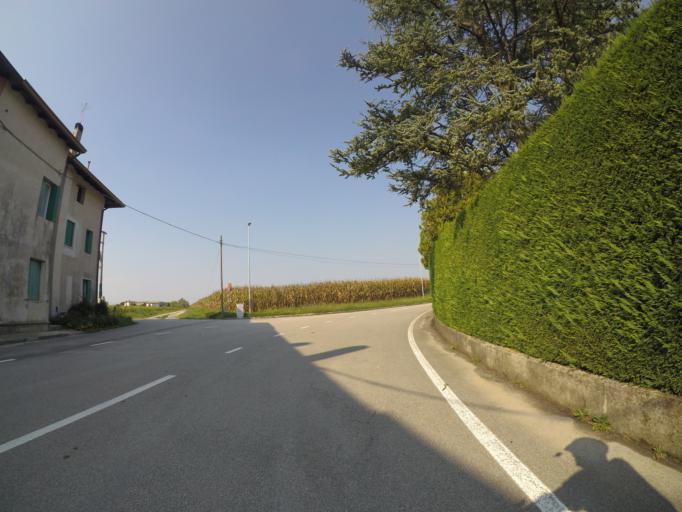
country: IT
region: Friuli Venezia Giulia
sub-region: Provincia di Udine
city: Camino al Tagliamento
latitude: 45.8972
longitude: 12.9542
